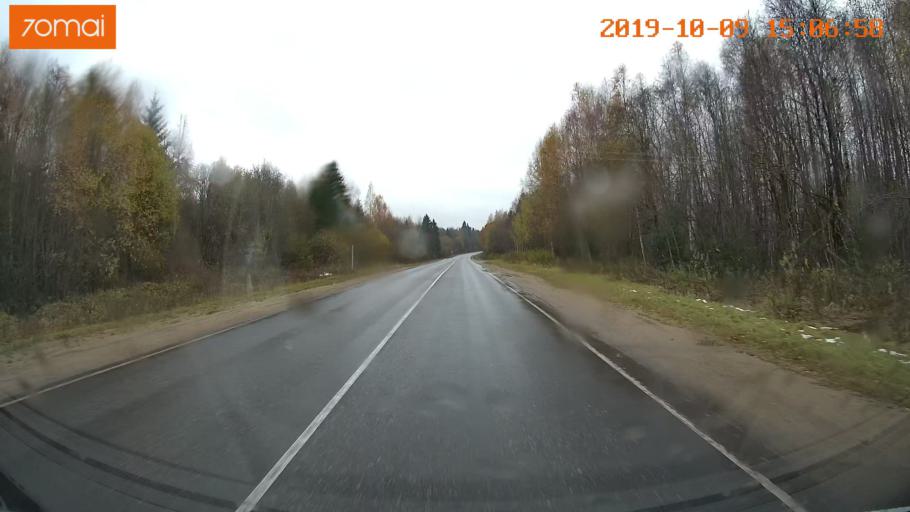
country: RU
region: Kostroma
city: Susanino
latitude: 58.2253
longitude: 41.6541
